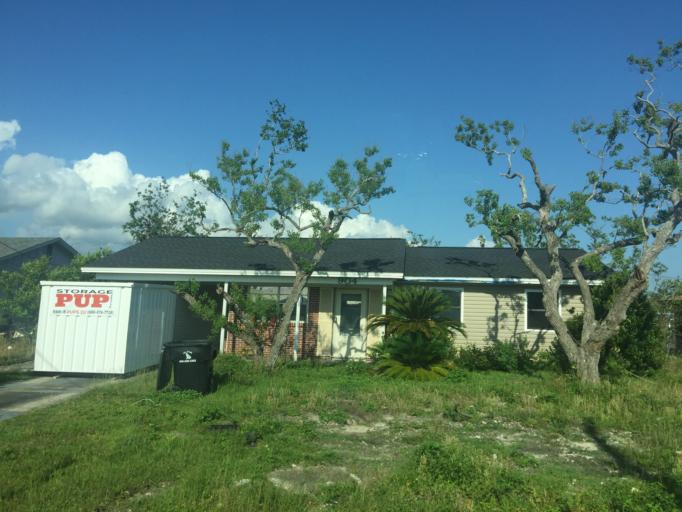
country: US
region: Florida
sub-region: Bay County
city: Cedar Grove
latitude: 30.1647
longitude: -85.6184
